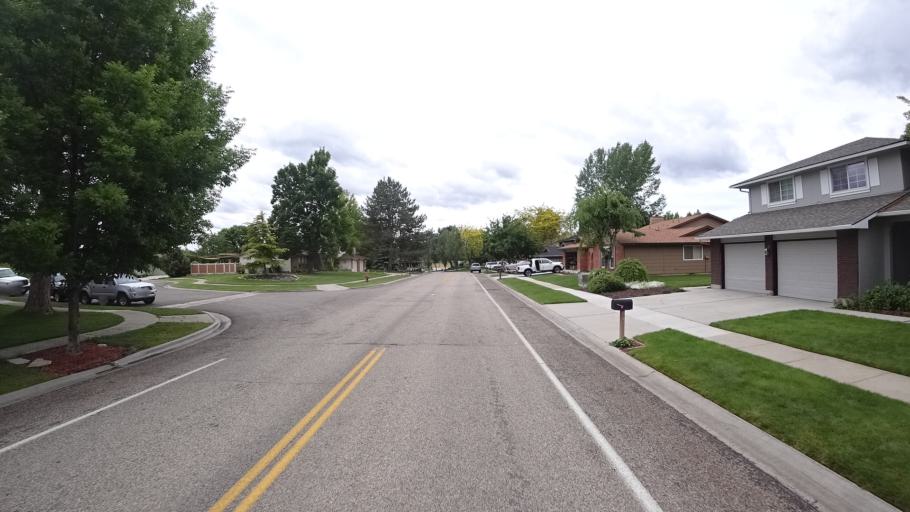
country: US
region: Idaho
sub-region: Ada County
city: Eagle
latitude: 43.7034
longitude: -116.3434
